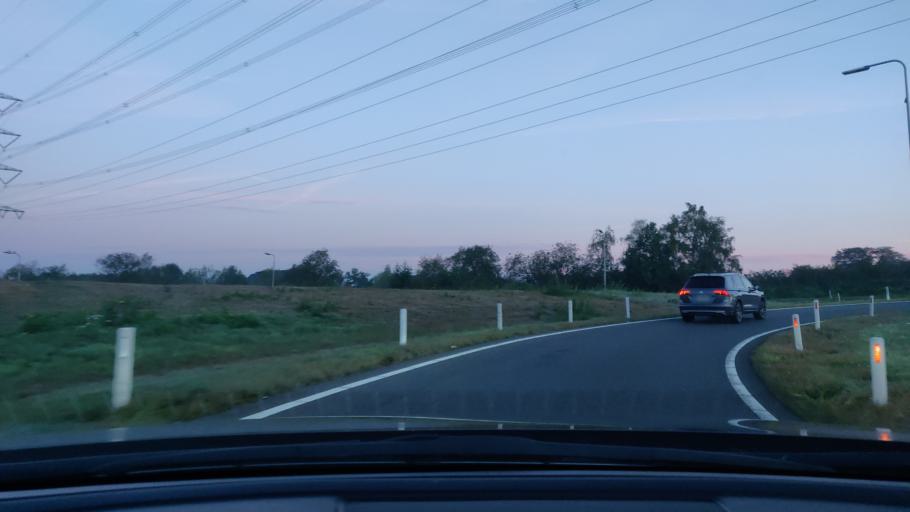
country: NL
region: Overijssel
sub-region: Gemeente Enschede
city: Enschede
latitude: 52.2007
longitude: 6.8872
